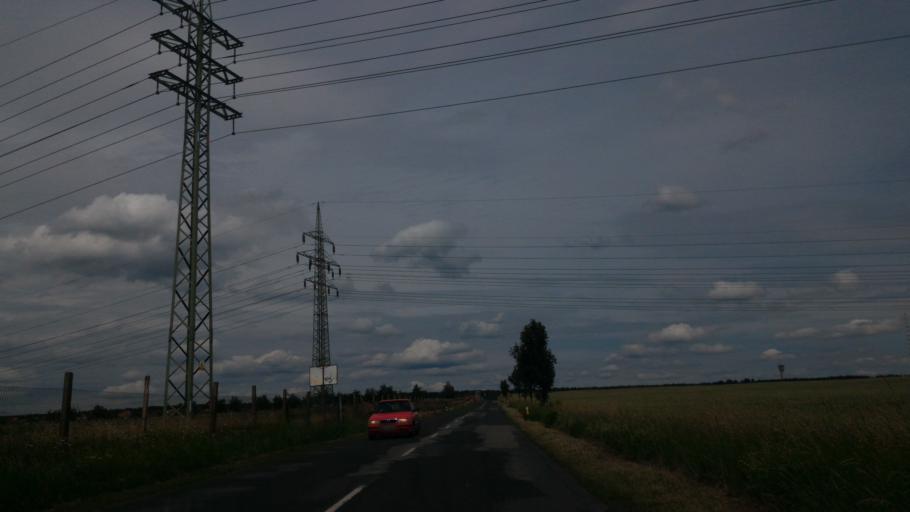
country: CZ
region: Central Bohemia
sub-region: Okres Melnik
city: Melnik
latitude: 50.3597
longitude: 14.5033
